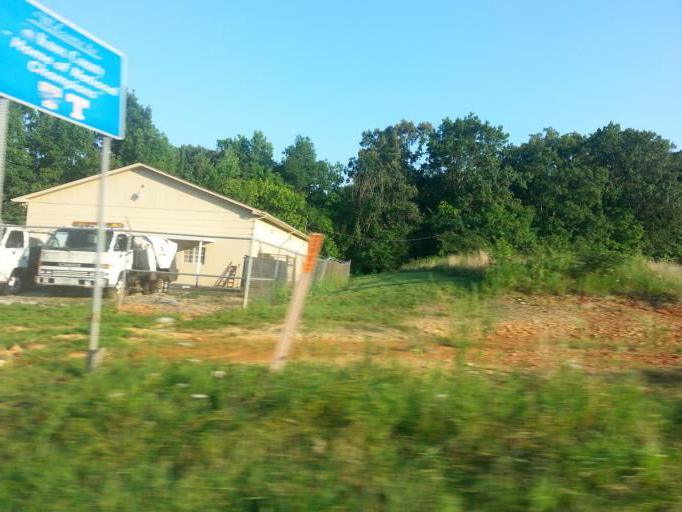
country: US
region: Tennessee
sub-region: Anderson County
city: Clinton
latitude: 36.0290
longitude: -84.0692
